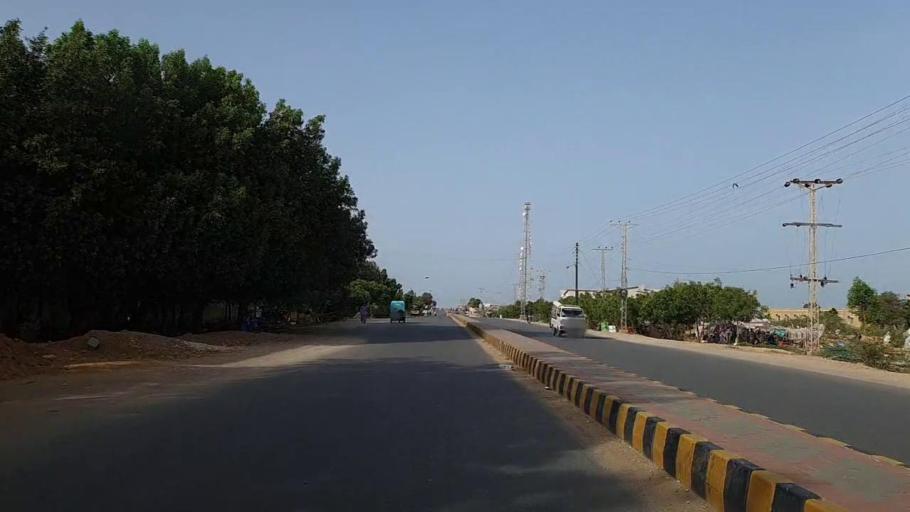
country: PK
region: Sindh
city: Thatta
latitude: 24.7480
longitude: 67.8957
